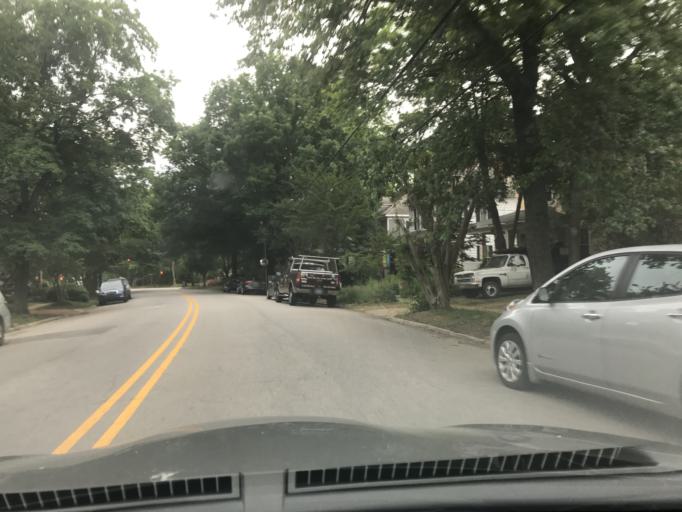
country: US
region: North Carolina
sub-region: Wake County
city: Raleigh
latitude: 35.7756
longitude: -78.6510
